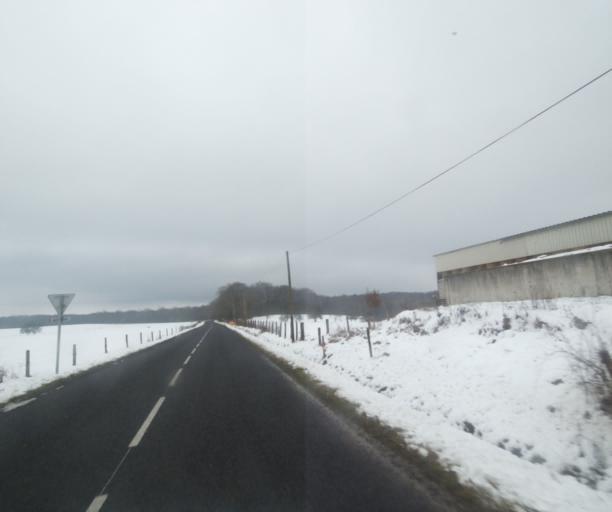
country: FR
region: Champagne-Ardenne
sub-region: Departement de la Haute-Marne
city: Laneuville-a-Remy
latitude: 48.4632
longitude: 4.9078
